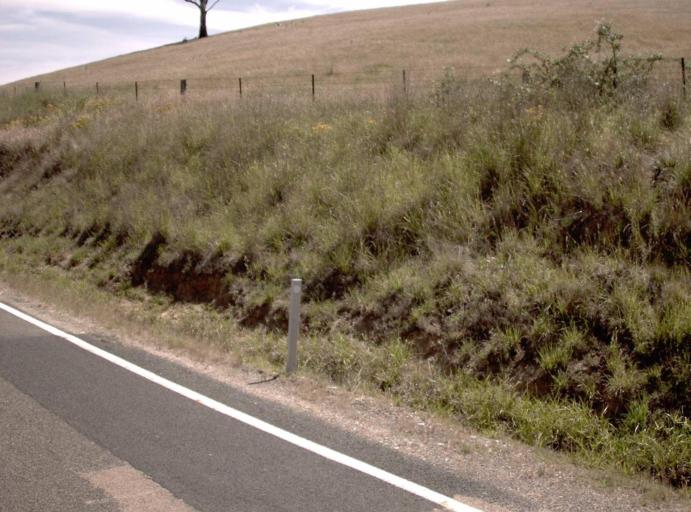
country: AU
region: Victoria
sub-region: Alpine
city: Mount Beauty
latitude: -37.0698
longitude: 147.6034
